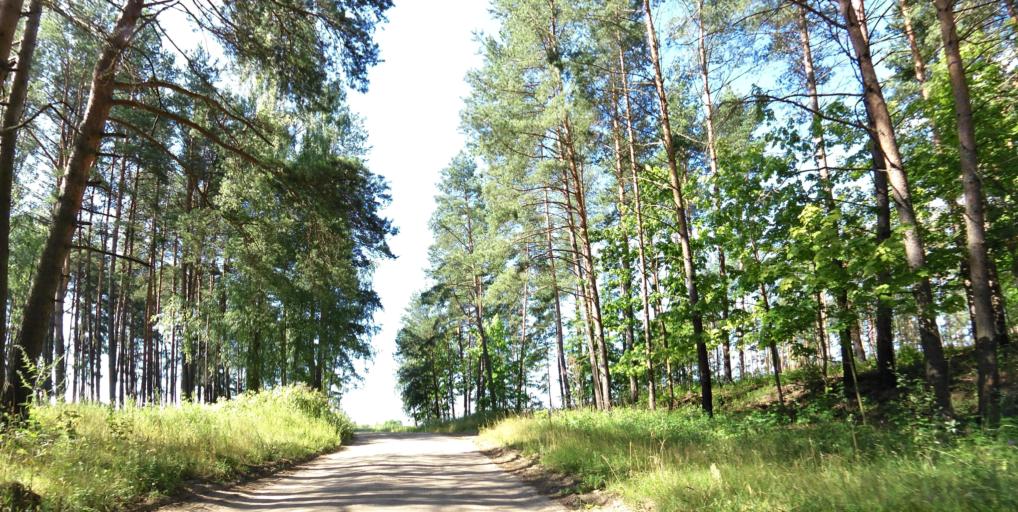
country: LT
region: Vilnius County
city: Pilaite
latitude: 54.6927
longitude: 25.1794
